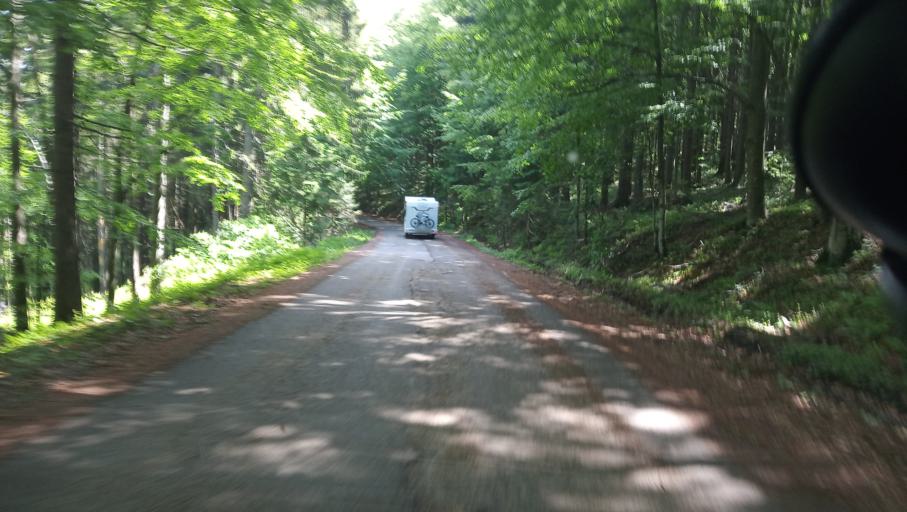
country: RO
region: Caras-Severin
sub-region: Comuna Valiug
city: Valiug
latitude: 45.2203
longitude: 22.0691
